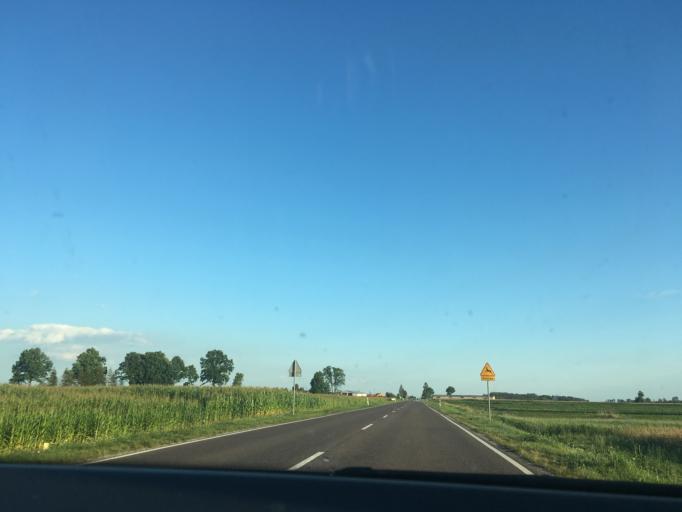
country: PL
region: Lublin Voivodeship
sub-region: Powiat bialski
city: Miedzyrzec Podlaski
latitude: 52.0453
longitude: 22.7453
